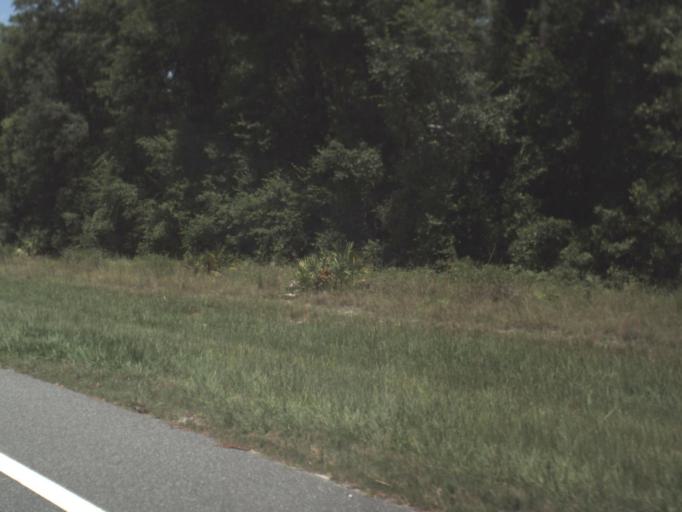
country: US
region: Florida
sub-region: Lafayette County
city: Mayo
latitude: 29.8880
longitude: -82.9550
